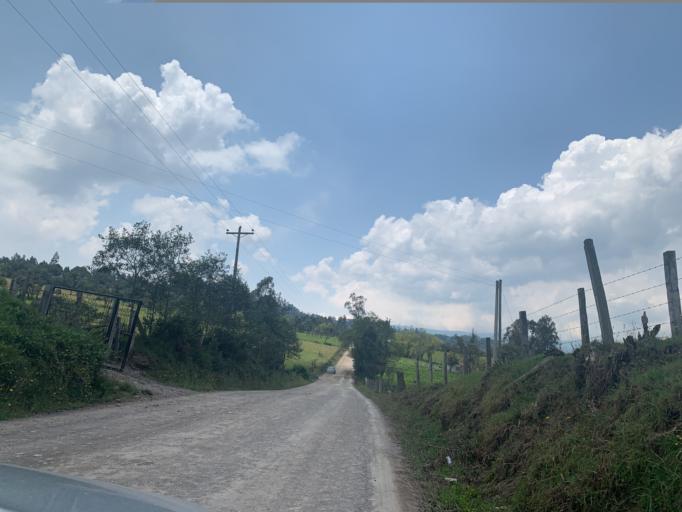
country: CO
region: Boyaca
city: Chiquinquira
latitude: 5.6012
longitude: -73.7645
